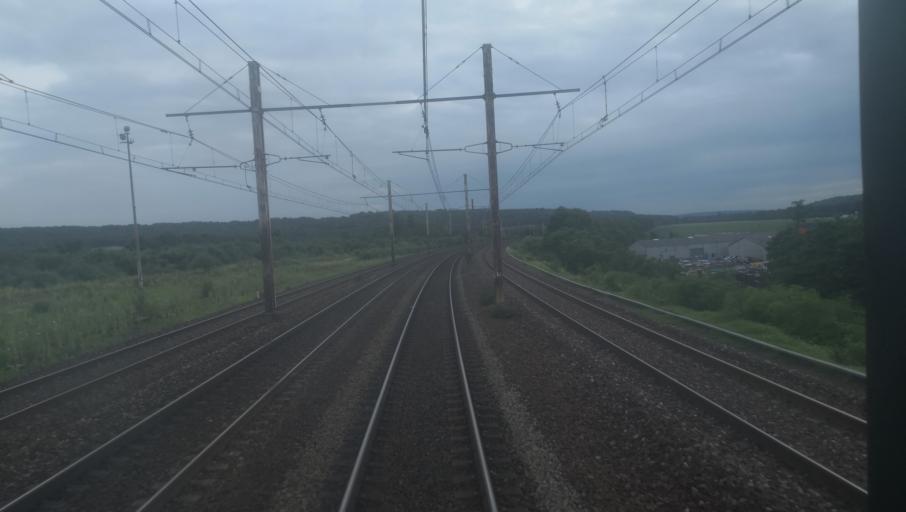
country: FR
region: Ile-de-France
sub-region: Departement de l'Essonne
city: Morigny-Champigny
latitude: 48.4565
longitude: 2.1688
